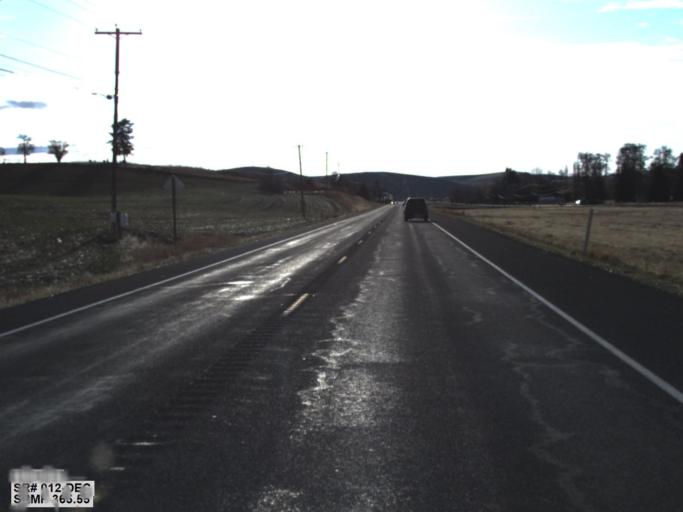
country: US
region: Washington
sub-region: Columbia County
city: Dayton
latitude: 46.3045
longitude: -118.0052
